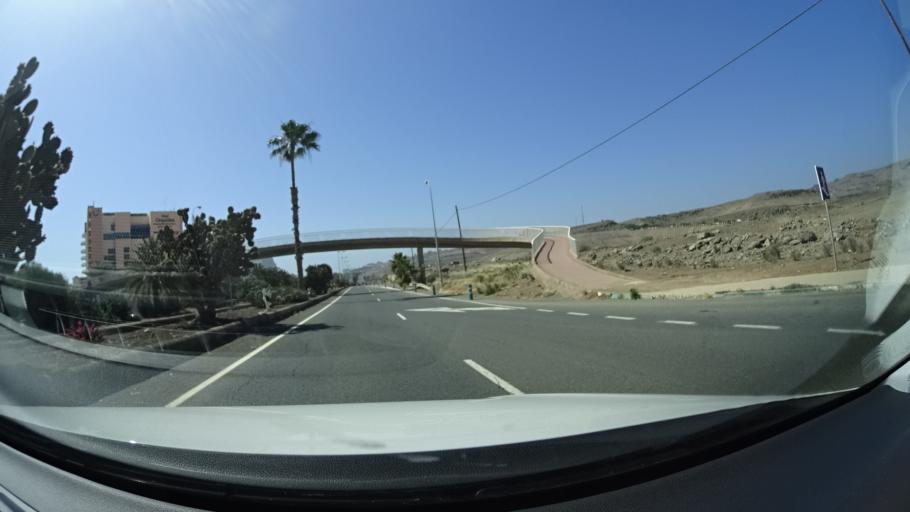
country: ES
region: Canary Islands
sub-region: Provincia de Las Palmas
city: Playa del Ingles
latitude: 27.7847
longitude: -15.5177
